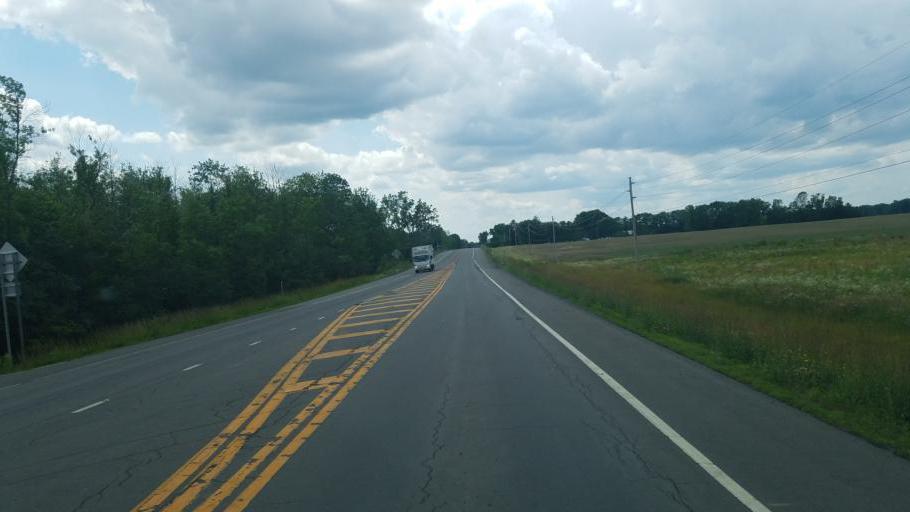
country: US
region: New York
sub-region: Seneca County
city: Waterloo
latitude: 42.9610
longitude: -76.8483
